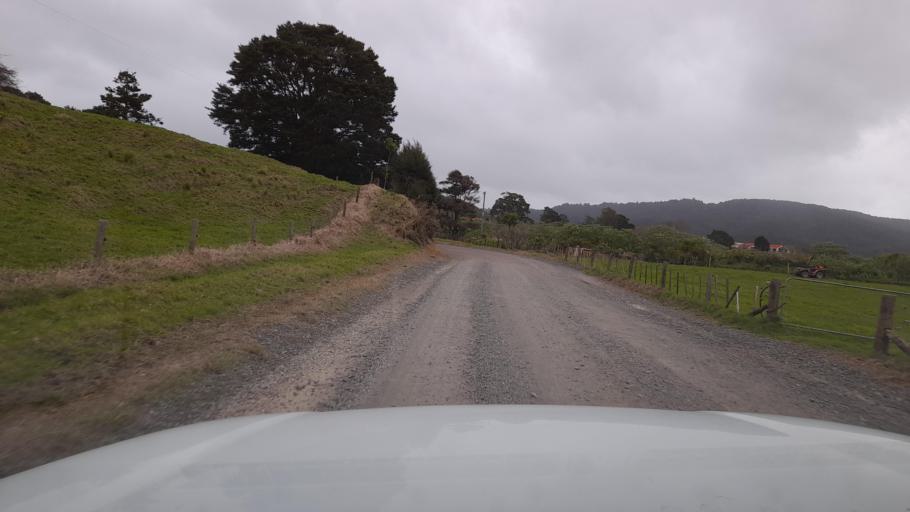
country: NZ
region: Northland
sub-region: Far North District
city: Paihia
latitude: -35.3423
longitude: 174.2307
